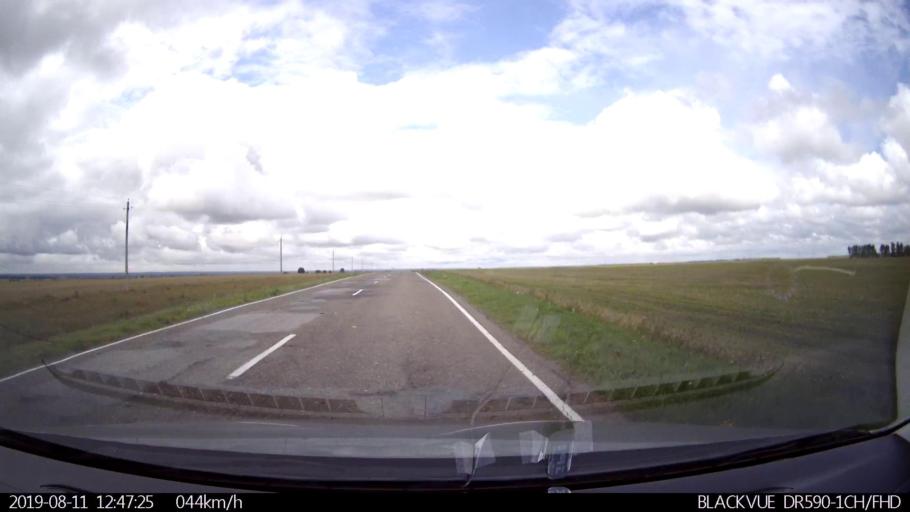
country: RU
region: Ulyanovsk
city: Ignatovka
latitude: 53.8693
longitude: 47.7088
